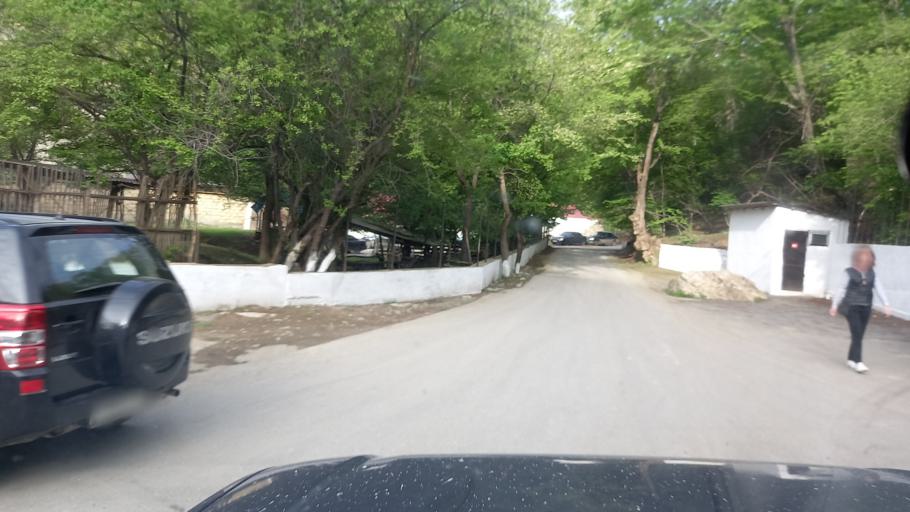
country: RU
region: Dagestan
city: Khuchni
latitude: 41.9725
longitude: 47.9288
